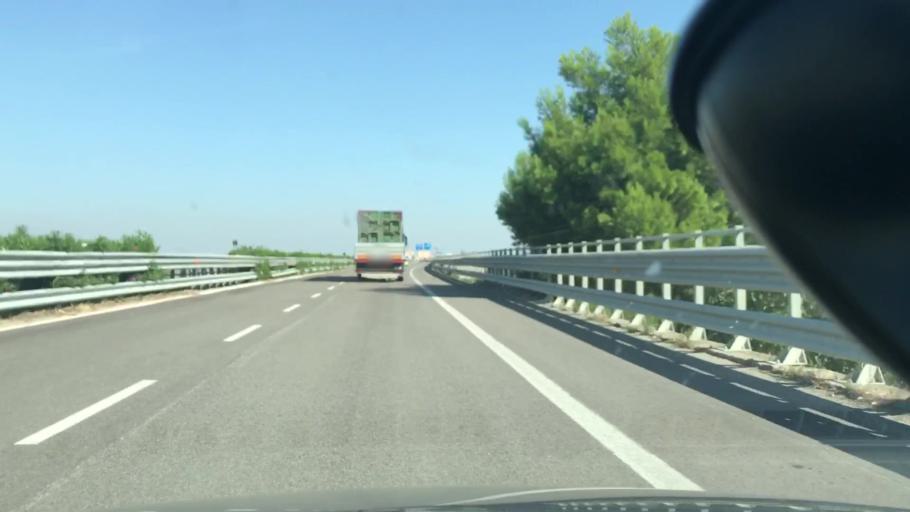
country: IT
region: Apulia
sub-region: Provincia di Foggia
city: Foggia
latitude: 41.4191
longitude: 15.5589
